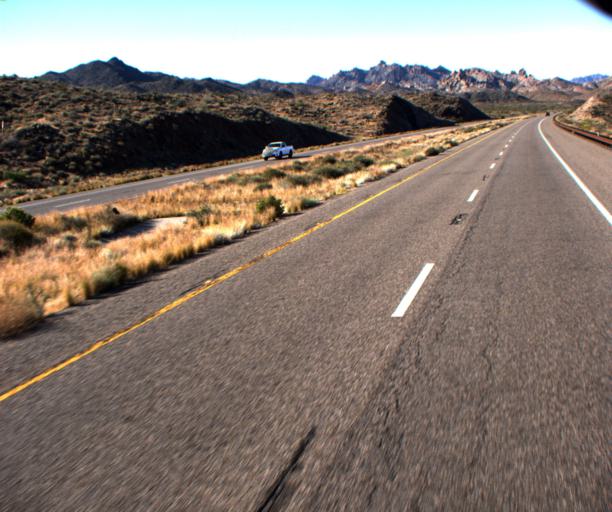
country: US
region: Nevada
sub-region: Clark County
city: Laughlin
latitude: 35.2037
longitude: -114.4036
